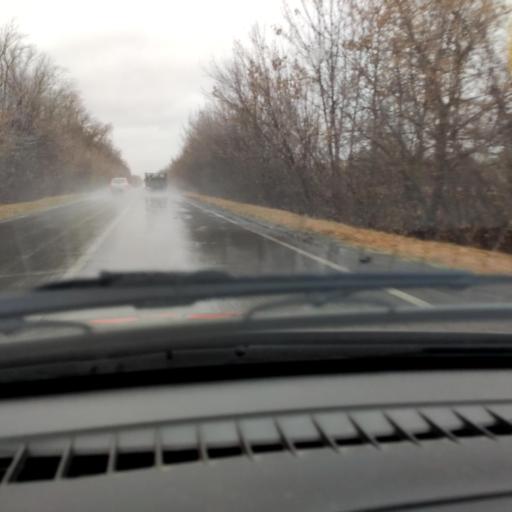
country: RU
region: Samara
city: Tol'yatti
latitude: 53.6907
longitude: 49.2502
